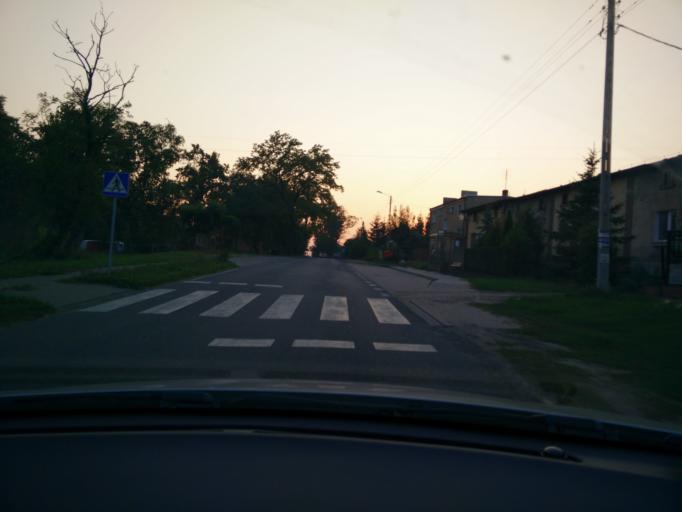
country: PL
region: Greater Poland Voivodeship
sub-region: Powiat sredzki
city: Dominowo
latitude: 52.2147
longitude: 17.3811
